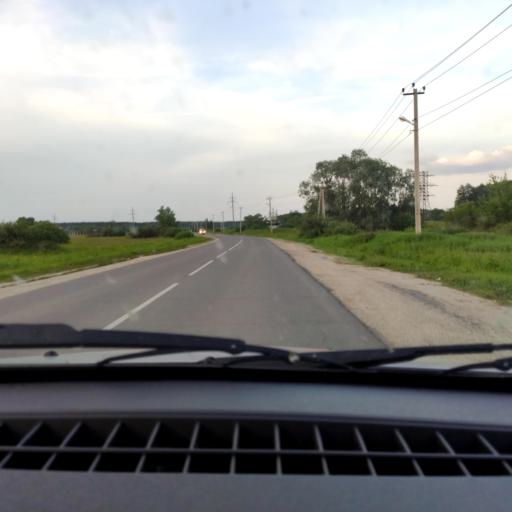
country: RU
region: Voronezj
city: Ramon'
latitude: 51.9502
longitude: 39.3871
